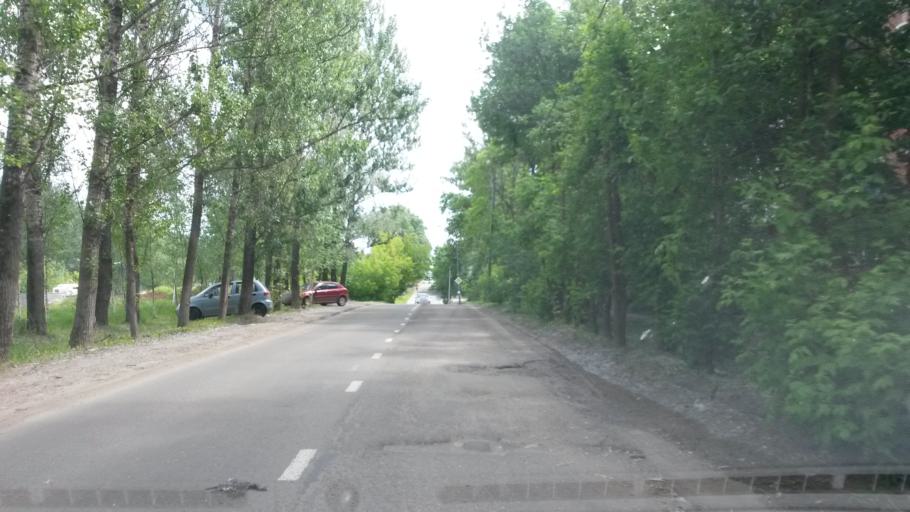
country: RU
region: Jaroslavl
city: Yaroslavl
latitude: 57.5877
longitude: 39.8365
